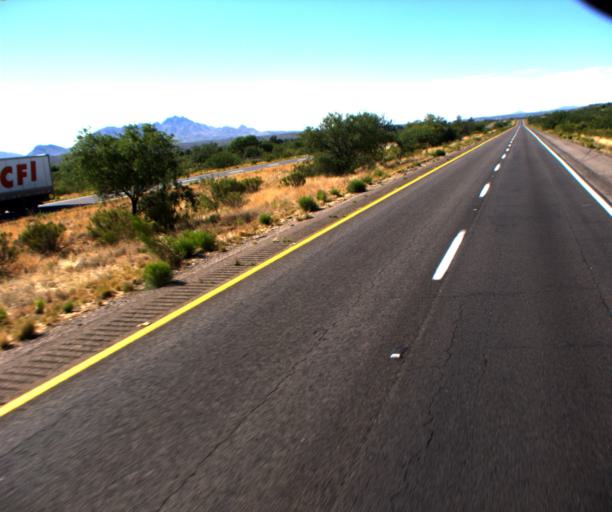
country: US
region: Arizona
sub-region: Santa Cruz County
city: Tubac
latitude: 31.6307
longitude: -111.0558
